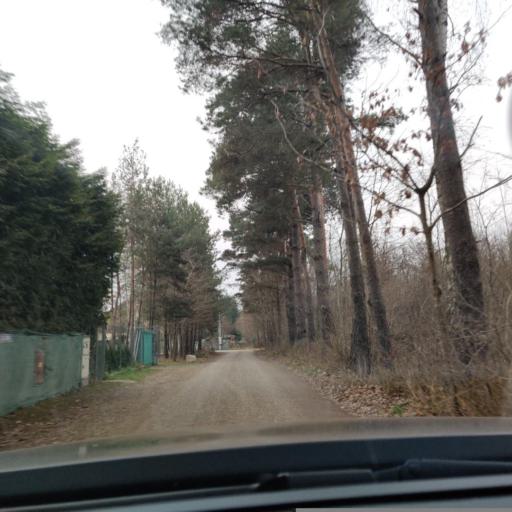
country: PL
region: Lodz Voivodeship
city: Zabia Wola
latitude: 52.0245
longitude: 20.6396
